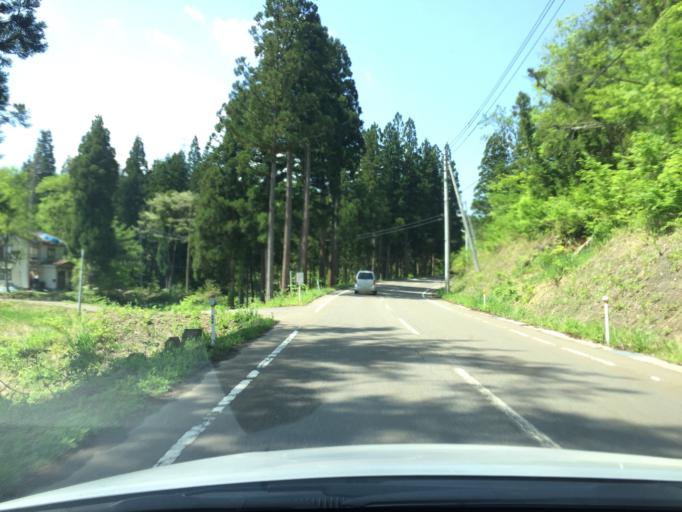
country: JP
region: Niigata
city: Tochio-honcho
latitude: 37.4696
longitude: 139.0353
